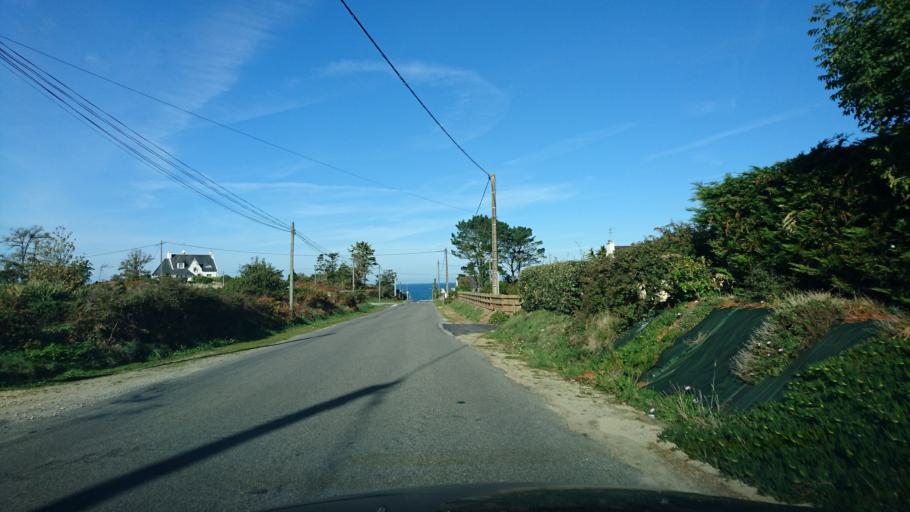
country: FR
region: Brittany
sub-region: Departement du Finistere
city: Lampaul-Plouarzel
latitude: 48.4333
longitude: -4.7710
